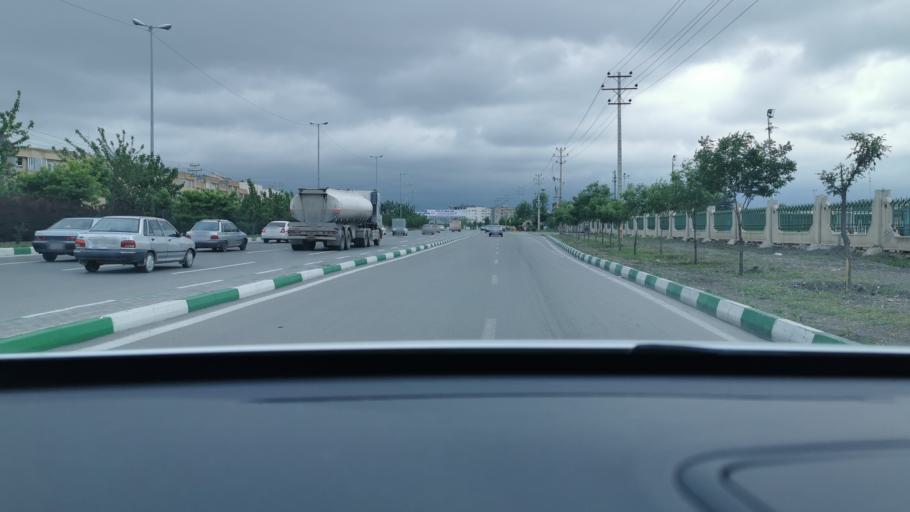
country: IR
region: Razavi Khorasan
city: Mashhad
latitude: 36.3777
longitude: 59.5079
